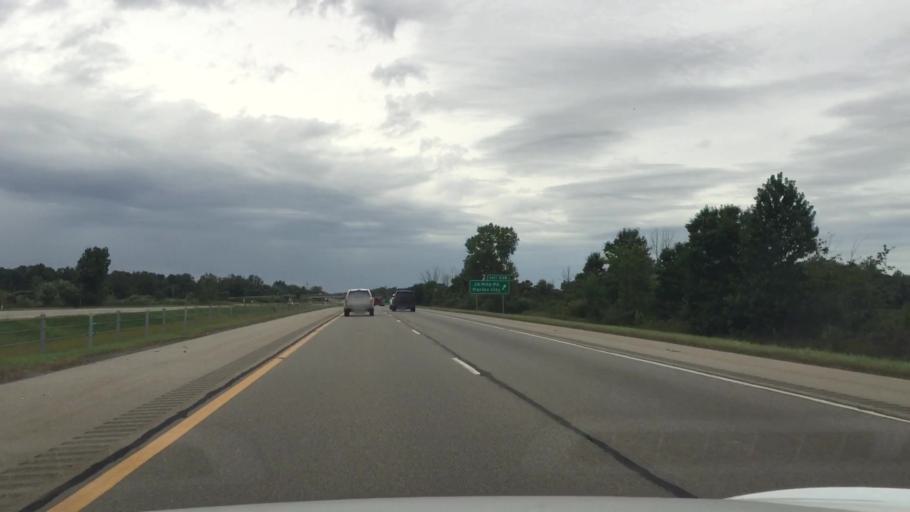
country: US
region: Michigan
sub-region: Macomb County
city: New Baltimore
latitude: 42.7249
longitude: -82.7462
